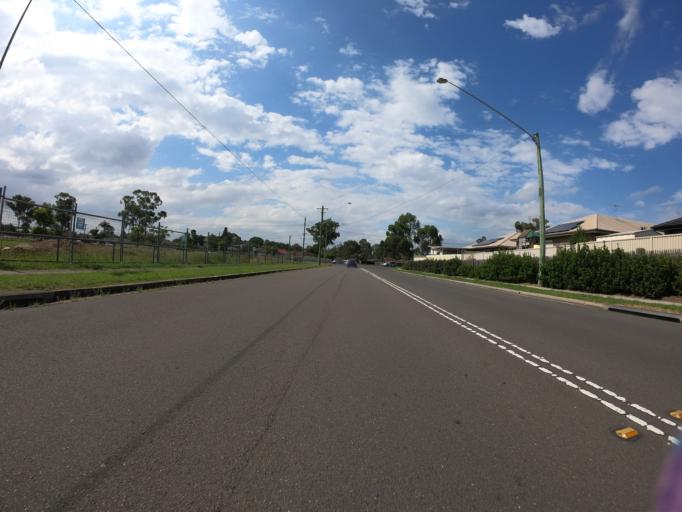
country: AU
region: New South Wales
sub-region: Blacktown
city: Blackett
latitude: -33.7447
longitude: 150.8282
